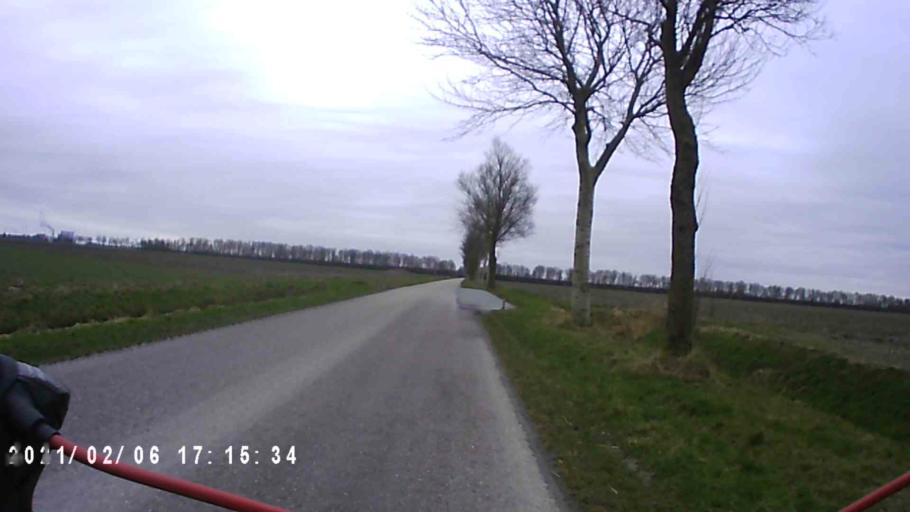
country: NL
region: Groningen
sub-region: Gemeente Appingedam
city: Appingedam
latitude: 53.4238
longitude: 6.7794
